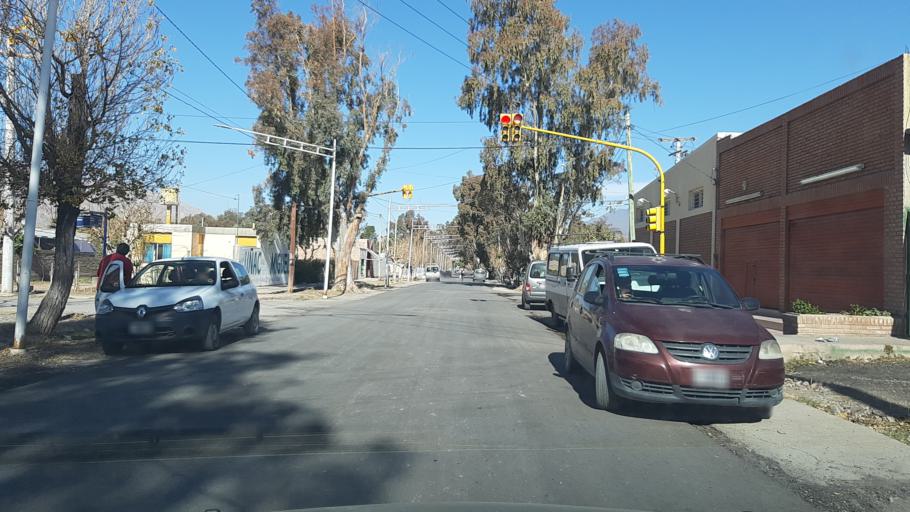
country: AR
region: San Juan
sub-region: Departamento de Zonda
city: Zonda
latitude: -31.5482
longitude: -68.7293
